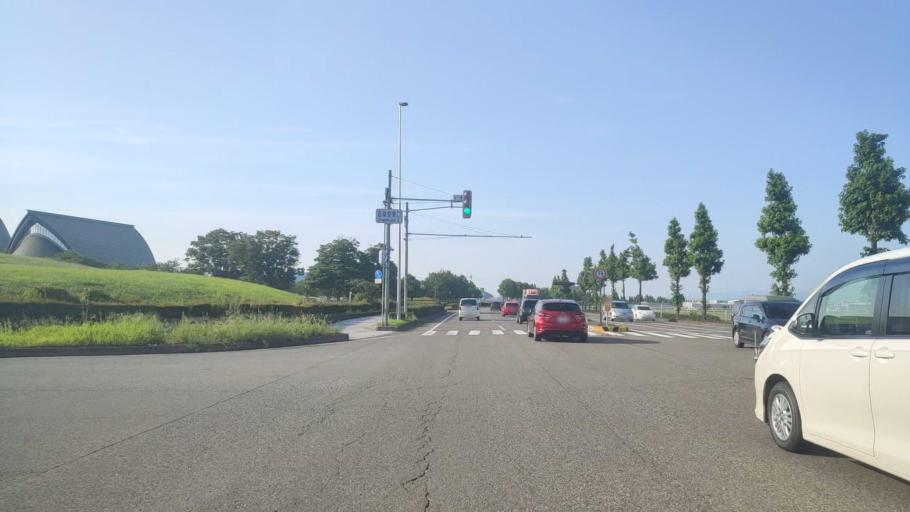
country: JP
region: Fukui
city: Fukui-shi
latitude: 36.0125
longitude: 136.2093
